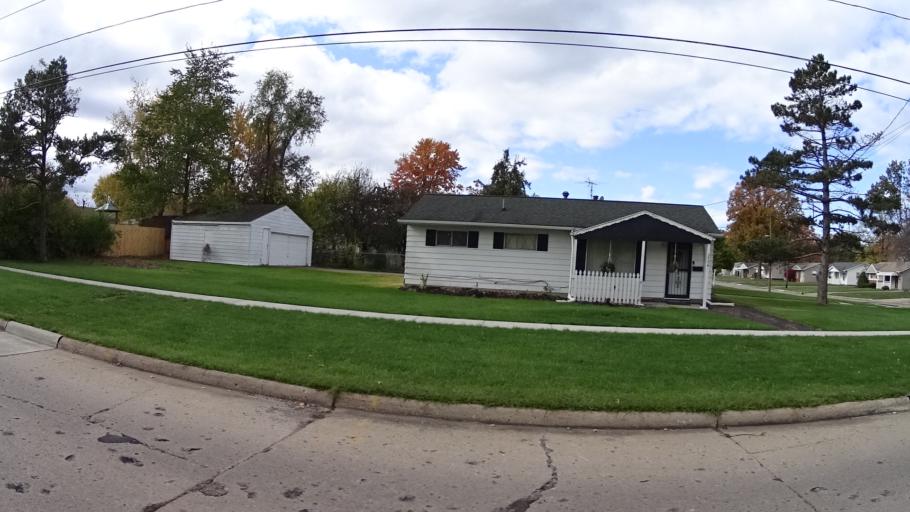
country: US
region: Ohio
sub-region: Lorain County
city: Sheffield
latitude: 41.4365
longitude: -82.1275
